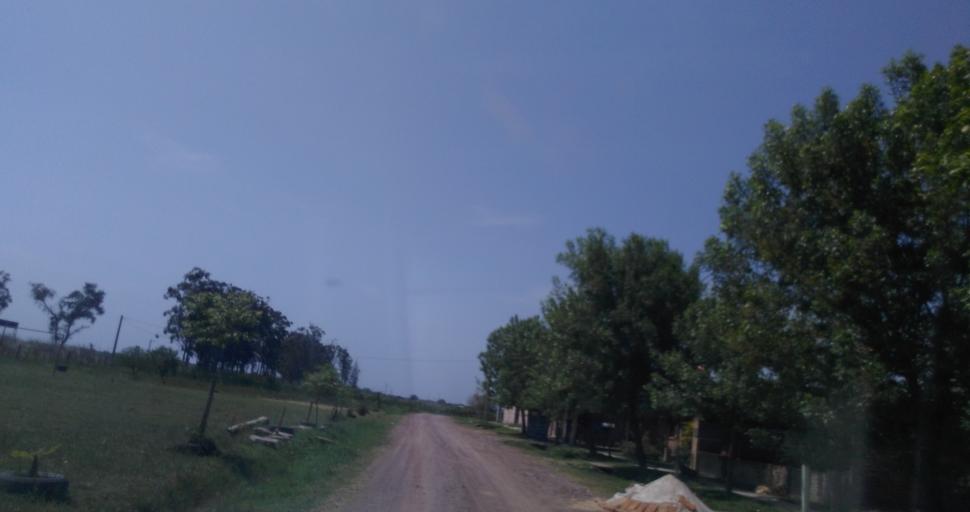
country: AR
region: Chaco
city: Fontana
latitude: -27.3958
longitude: -59.0003
